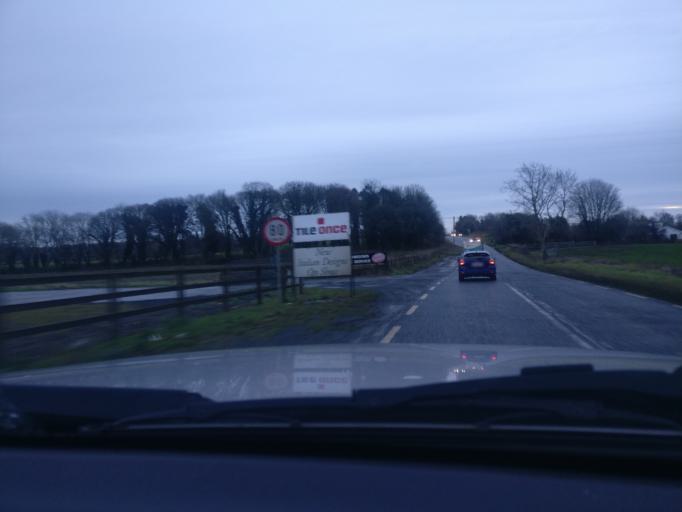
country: IE
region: Leinster
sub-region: An Mhi
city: Kells
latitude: 53.7114
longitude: -6.8152
